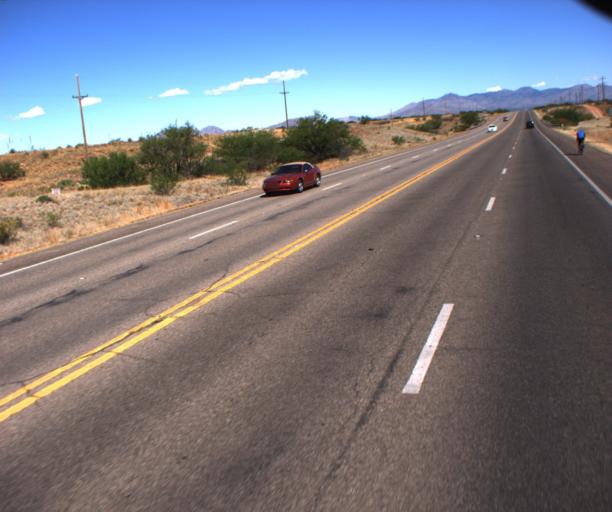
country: US
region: Arizona
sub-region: Cochise County
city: Sierra Vista
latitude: 31.5790
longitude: -110.3175
